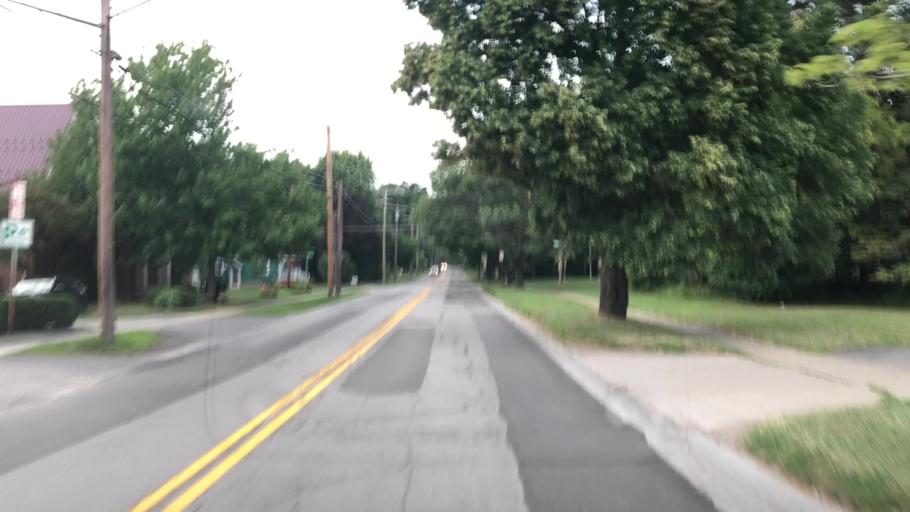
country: US
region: New York
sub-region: Erie County
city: East Aurora
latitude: 42.7686
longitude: -78.6078
